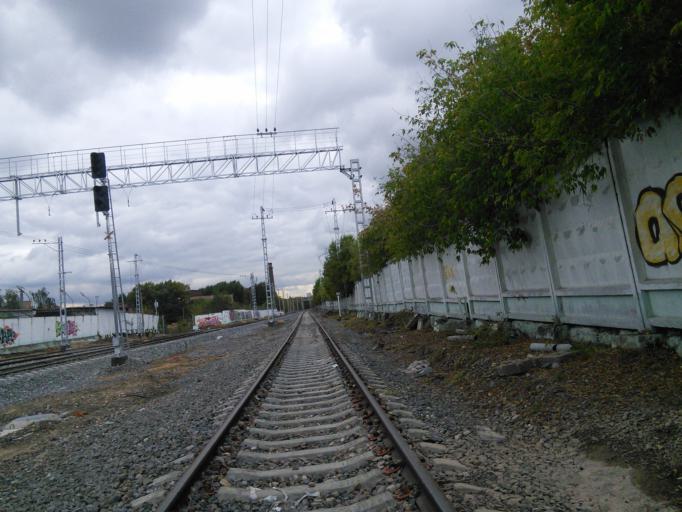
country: RU
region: Moskovskaya
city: Kozhukhovo
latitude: 55.6969
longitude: 37.6457
